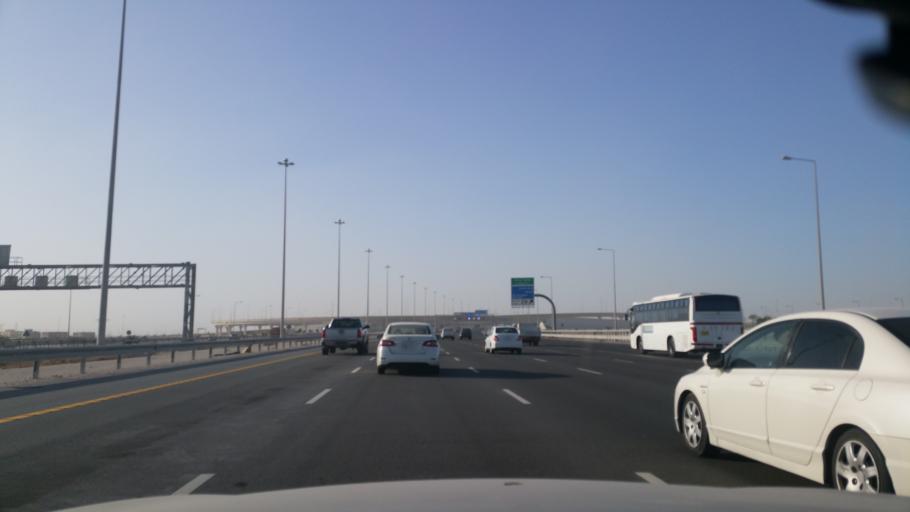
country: QA
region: Al Wakrah
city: Al Wukayr
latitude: 25.1766
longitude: 51.5531
